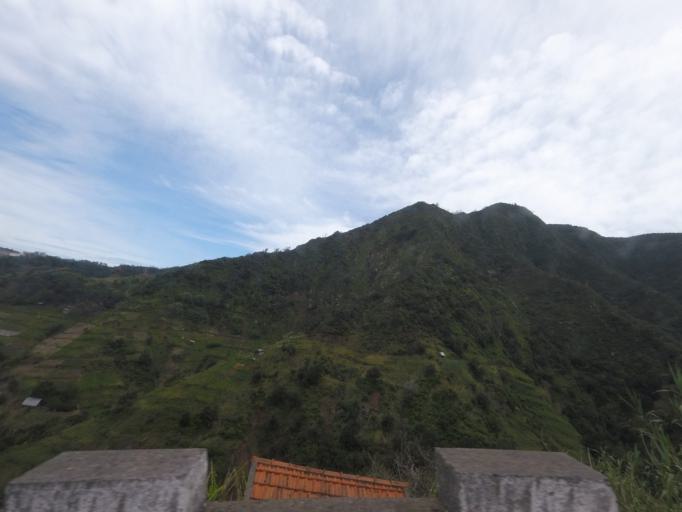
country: PT
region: Madeira
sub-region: Santa Cruz
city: Santa Cruz
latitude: 32.7568
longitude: -16.8199
